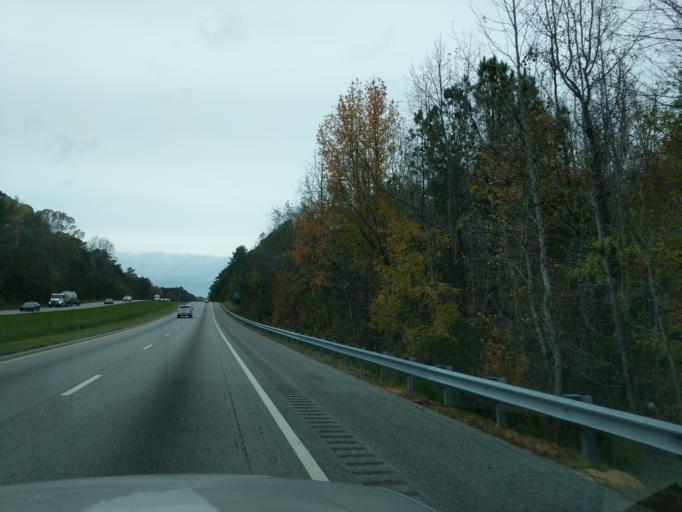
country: US
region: South Carolina
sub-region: Laurens County
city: Joanna
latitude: 34.4460
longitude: -81.7721
